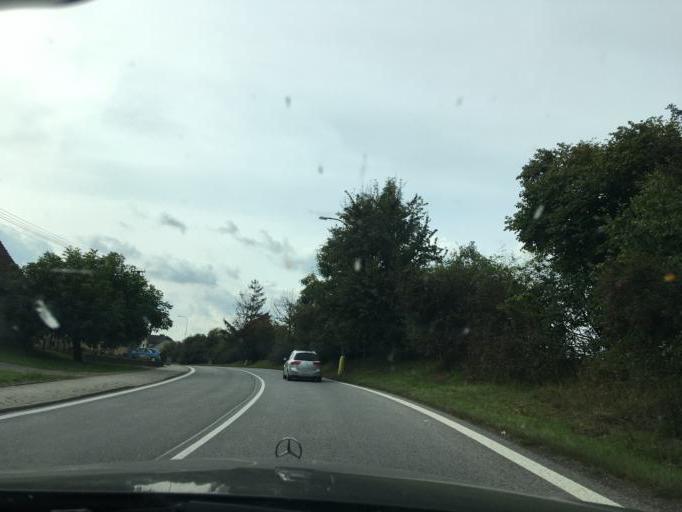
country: CZ
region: Kralovehradecky
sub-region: Okres Nachod
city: Ceska Skalice
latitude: 50.3923
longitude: 15.9893
